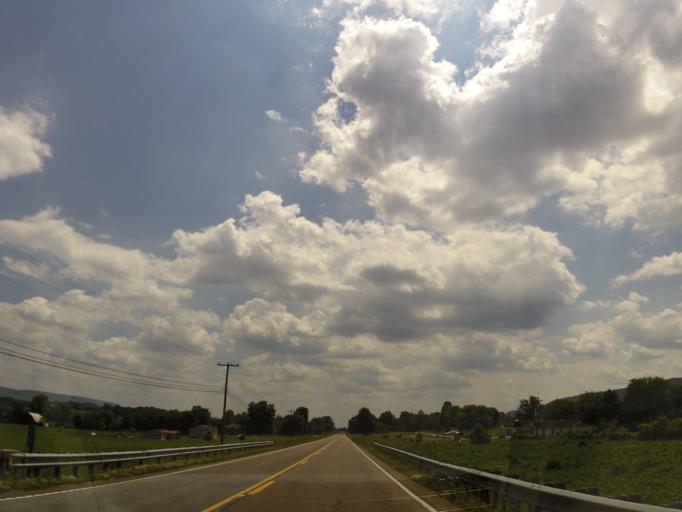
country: US
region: Tennessee
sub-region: Bledsoe County
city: Pikeville
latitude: 35.5626
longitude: -85.2467
